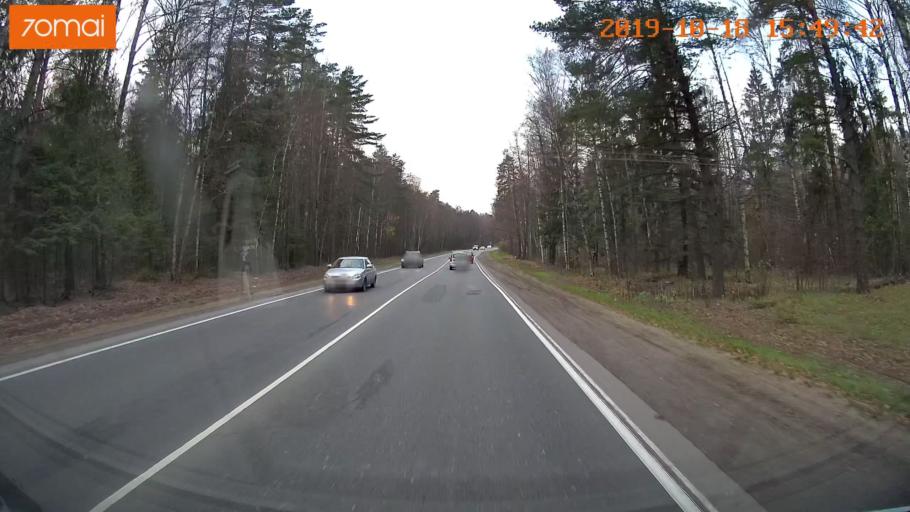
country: RU
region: Vladimir
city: Kommunar
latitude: 56.0263
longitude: 40.5714
